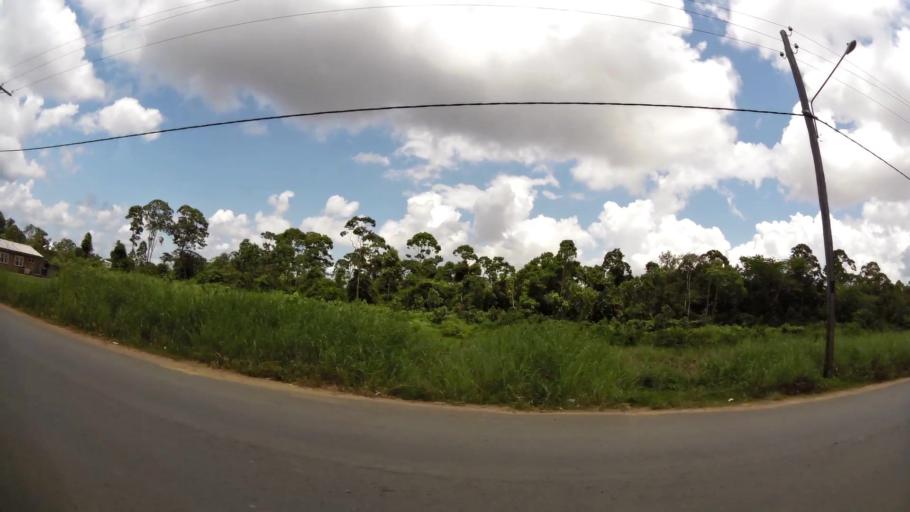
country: SR
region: Paramaribo
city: Paramaribo
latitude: 5.8022
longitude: -55.1238
